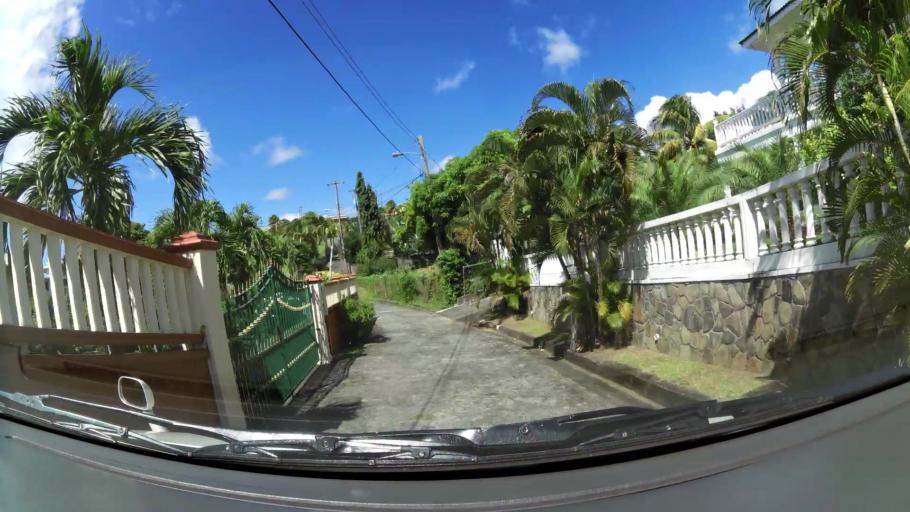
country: VC
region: Saint George
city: Kingstown
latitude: 13.1391
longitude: -61.2250
